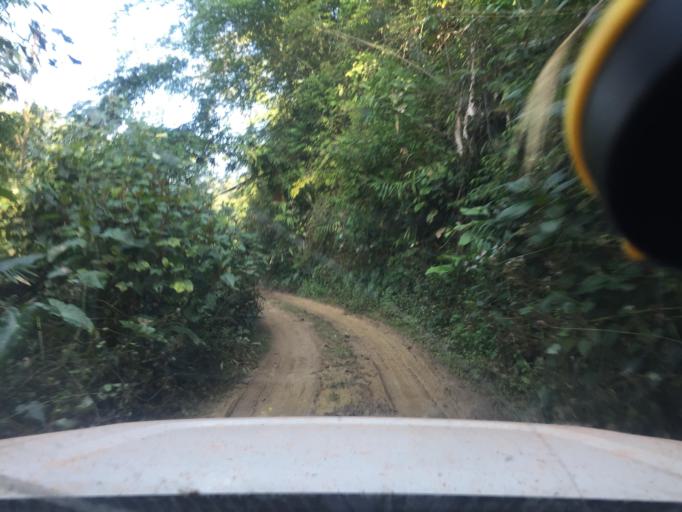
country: LA
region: Phongsali
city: Phongsali
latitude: 21.7027
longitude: 102.3941
